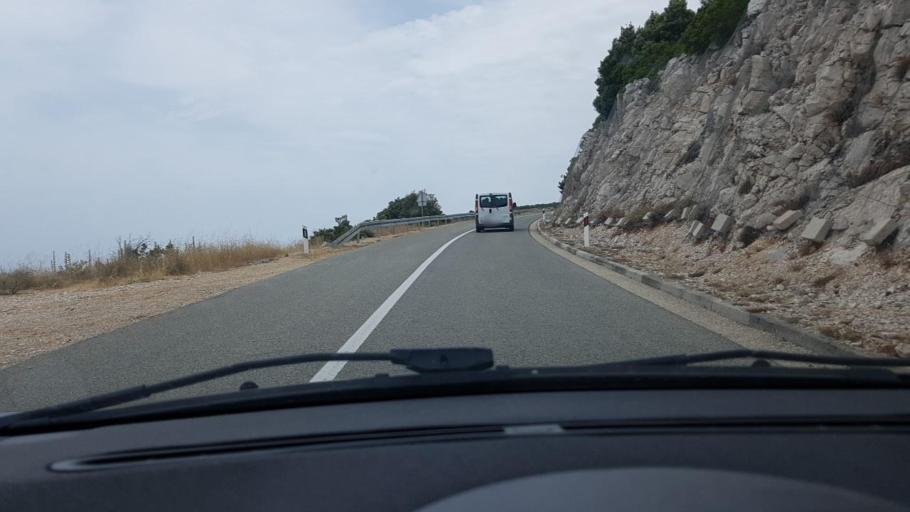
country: HR
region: Dubrovacko-Neretvanska
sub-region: Grad Korcula
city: Zrnovo
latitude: 42.9389
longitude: 17.0112
